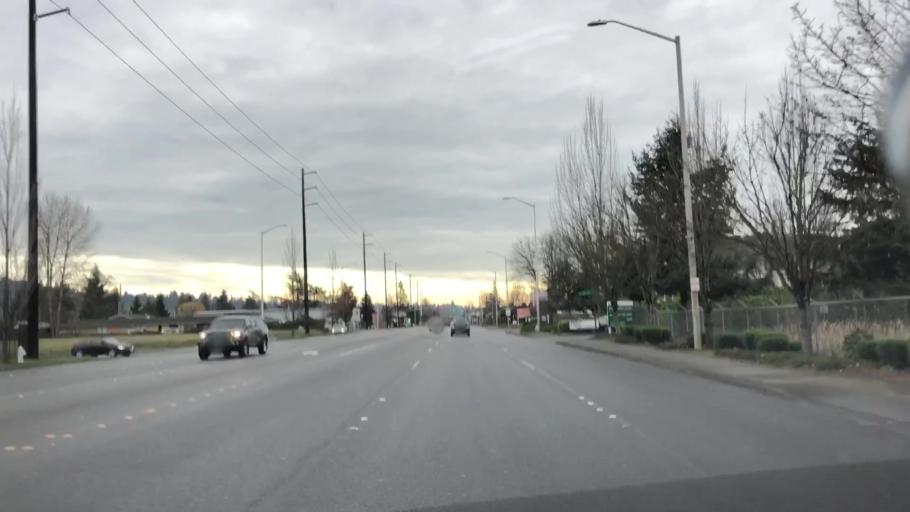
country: US
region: Washington
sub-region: King County
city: Kent
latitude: 47.4074
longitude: -122.2281
